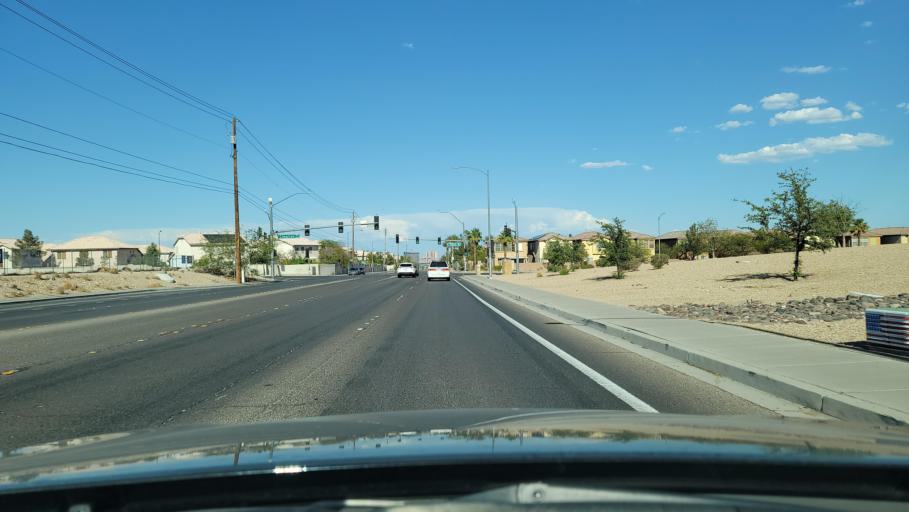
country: US
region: Nevada
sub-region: Clark County
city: Spring Valley
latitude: 36.1257
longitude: -115.2712
